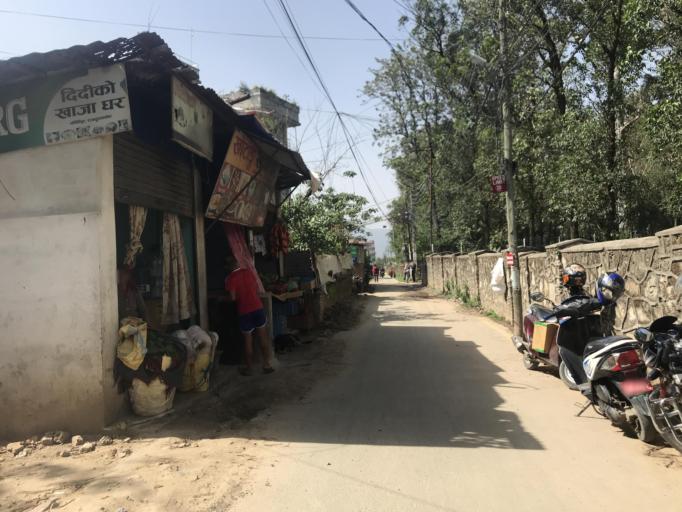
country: NP
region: Central Region
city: Kirtipur
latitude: 27.6807
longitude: 85.2816
